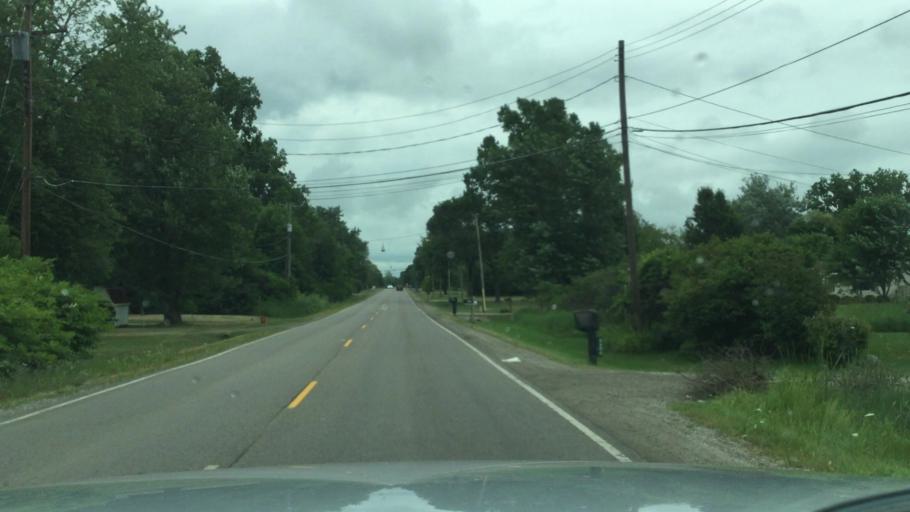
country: US
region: Michigan
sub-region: Genesee County
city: Beecher
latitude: 43.0768
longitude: -83.6365
